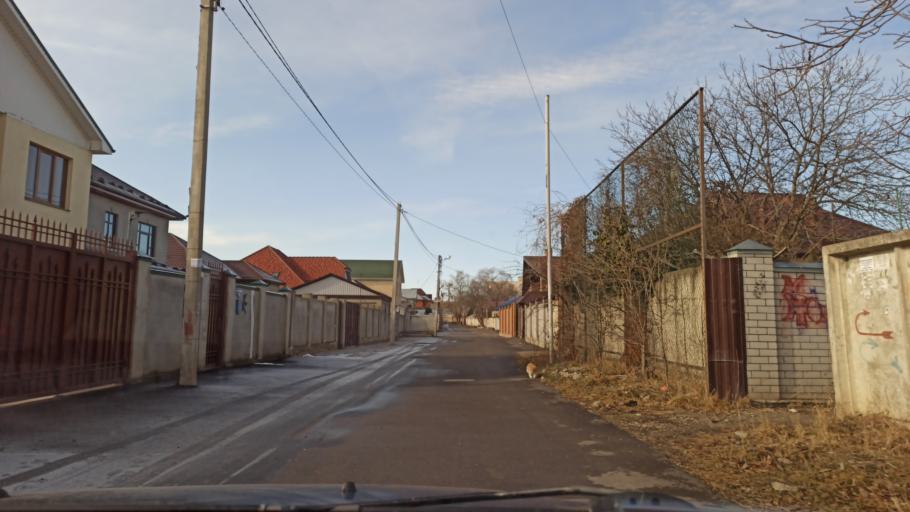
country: RU
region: Stavropol'skiy
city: Yessentukskaya
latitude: 44.0373
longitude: 42.8782
